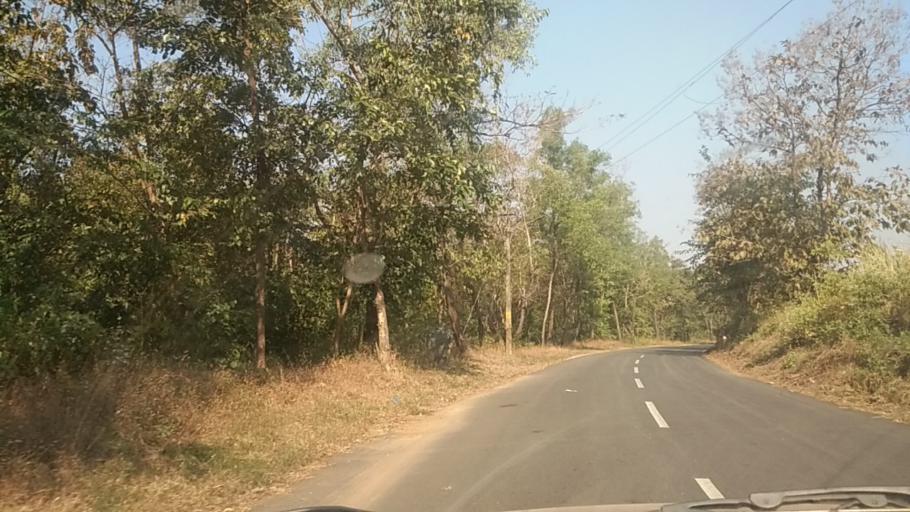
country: IN
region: Goa
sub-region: South Goa
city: Sanguem
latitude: 15.2036
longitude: 74.2216
